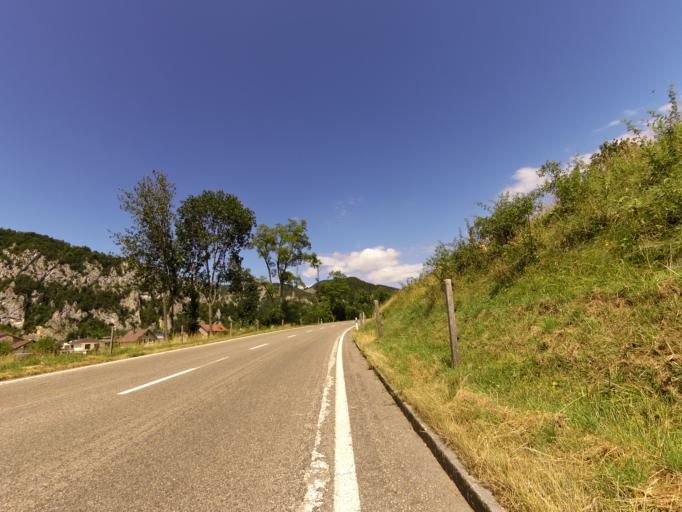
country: CH
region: Solothurn
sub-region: Bezirk Thal
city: Balsthal
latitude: 47.3165
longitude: 7.7035
